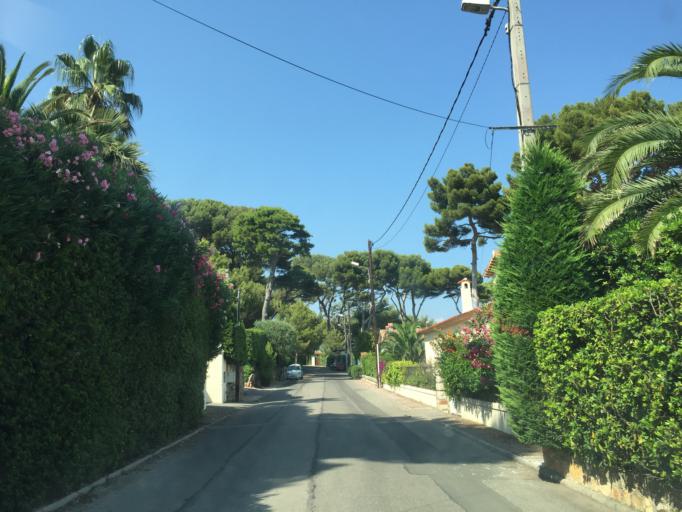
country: FR
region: Provence-Alpes-Cote d'Azur
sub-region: Departement des Alpes-Maritimes
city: Antibes
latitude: 43.5658
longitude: 7.1364
